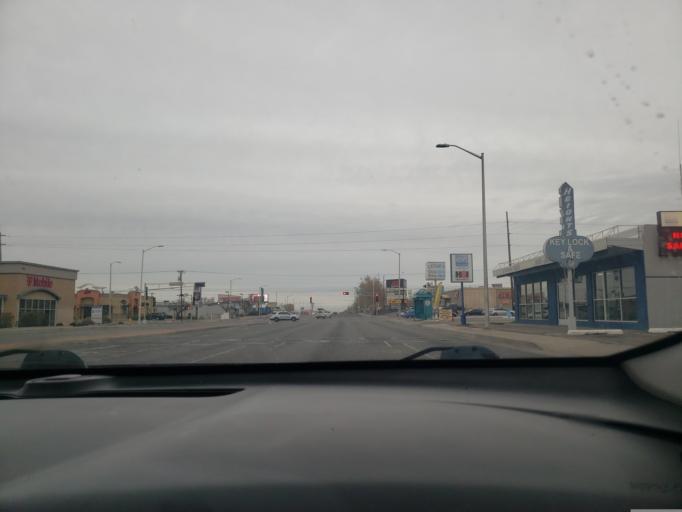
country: US
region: New Mexico
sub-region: Bernalillo County
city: Albuquerque
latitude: 35.0865
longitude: -106.5861
